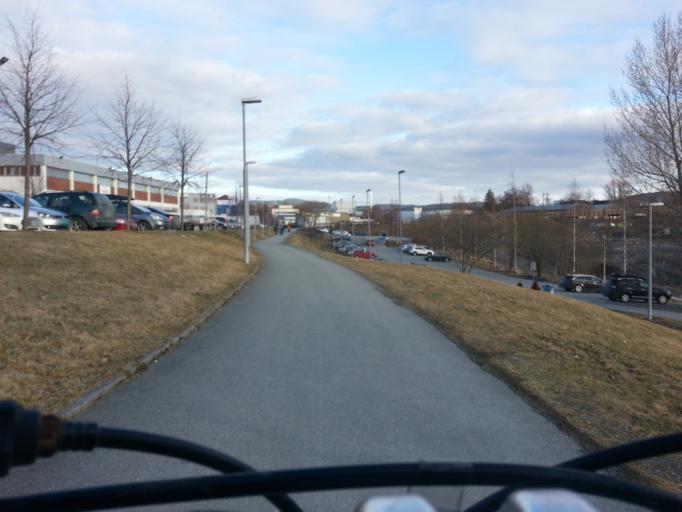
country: NO
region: Sor-Trondelag
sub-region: Trondheim
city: Trondheim
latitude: 63.4426
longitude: 10.4457
